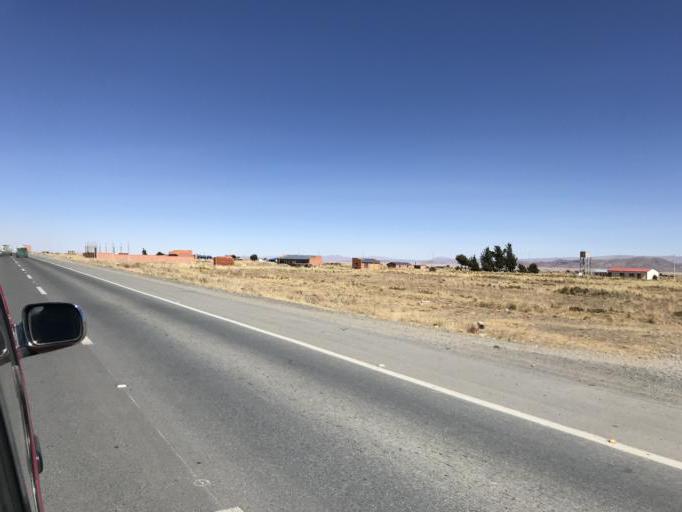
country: BO
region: La Paz
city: Batallas
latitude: -16.3490
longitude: -68.4040
